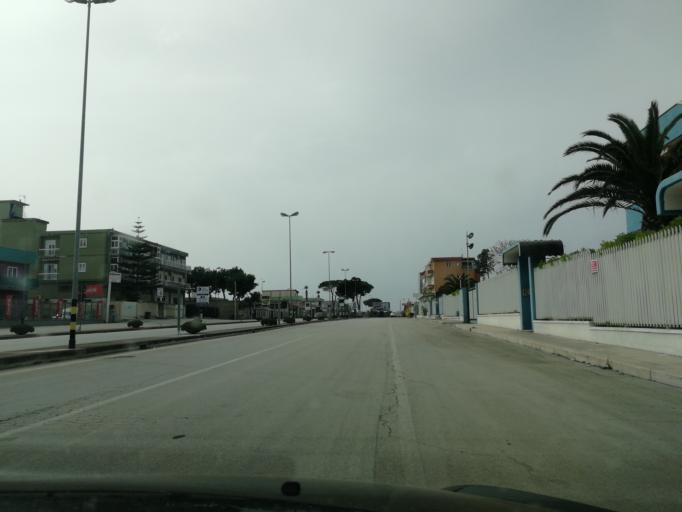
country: IT
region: Apulia
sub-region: Provincia di Barletta - Andria - Trani
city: Barletta
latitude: 41.3106
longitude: 16.3091
